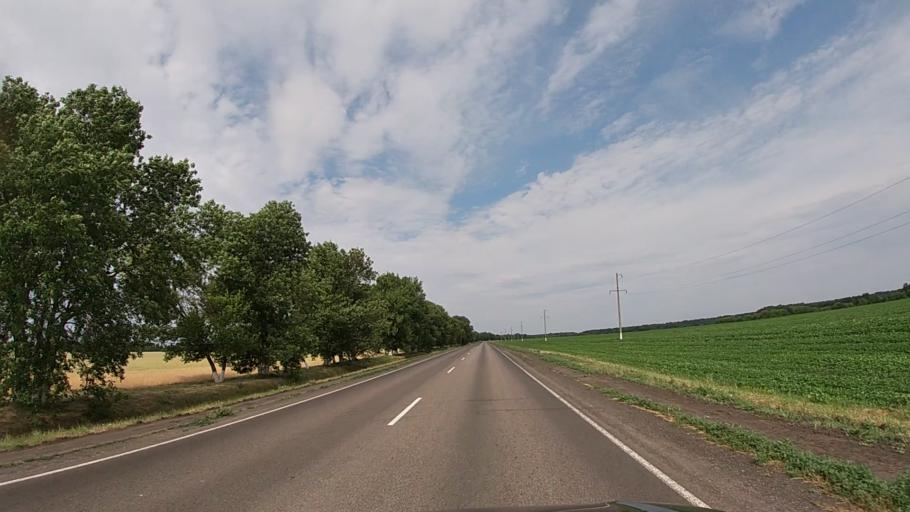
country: RU
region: Belgorod
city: Krasnaya Yaruga
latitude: 50.8082
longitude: 35.5338
